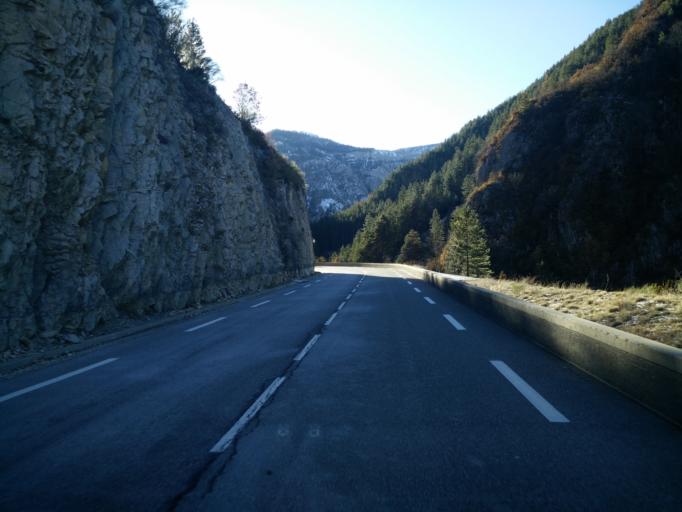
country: FR
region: Provence-Alpes-Cote d'Azur
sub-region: Departement des Alpes-de-Haute-Provence
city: Annot
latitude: 43.9508
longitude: 6.6872
